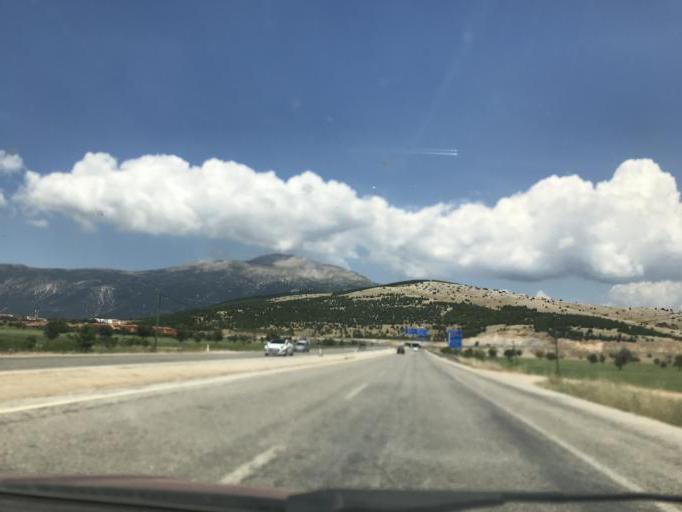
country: TR
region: Denizli
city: Serinhisar
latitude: 37.6271
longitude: 29.2105
